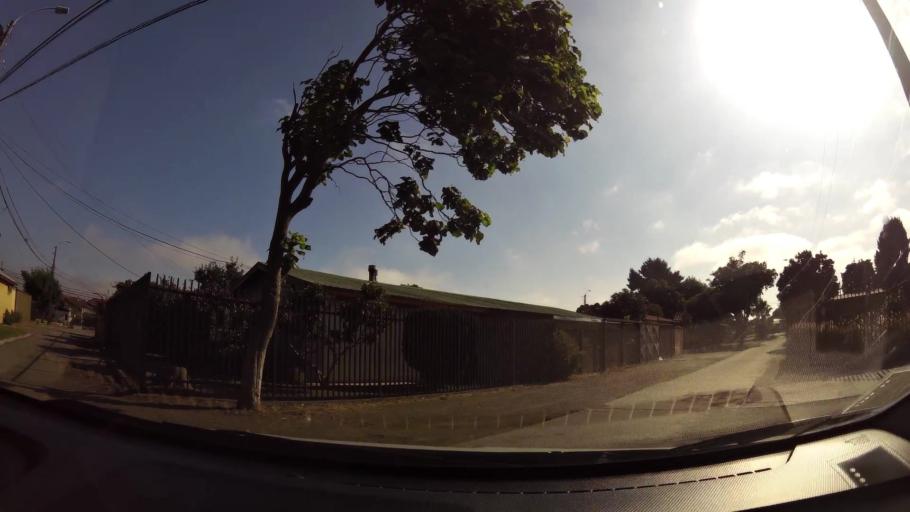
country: CL
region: Biobio
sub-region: Provincia de Concepcion
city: Concepcion
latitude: -36.7973
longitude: -73.0883
